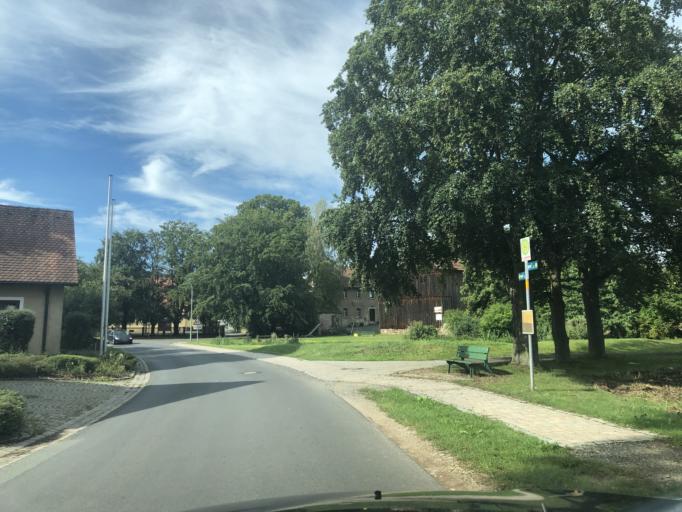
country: DE
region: Bavaria
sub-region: Upper Palatinate
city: Trabitz
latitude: 49.7968
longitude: 11.8785
